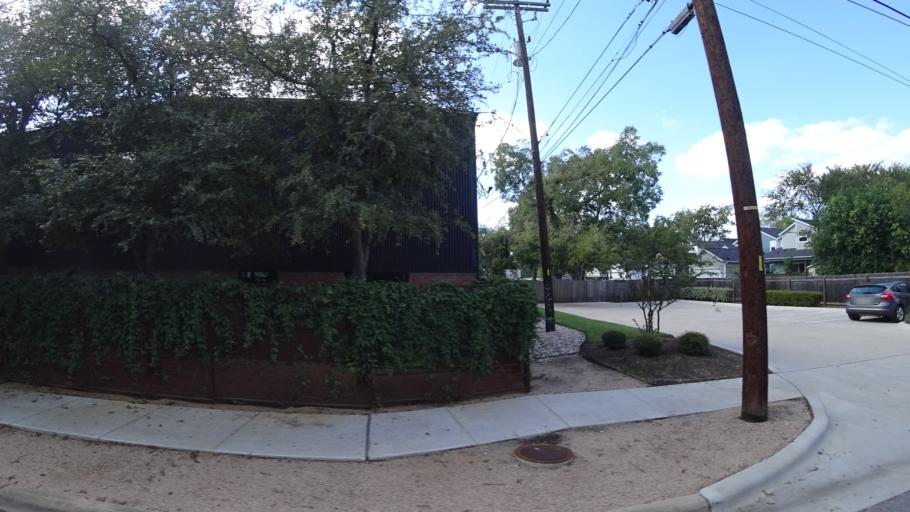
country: US
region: Texas
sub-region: Travis County
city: Austin
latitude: 30.3099
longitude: -97.7143
